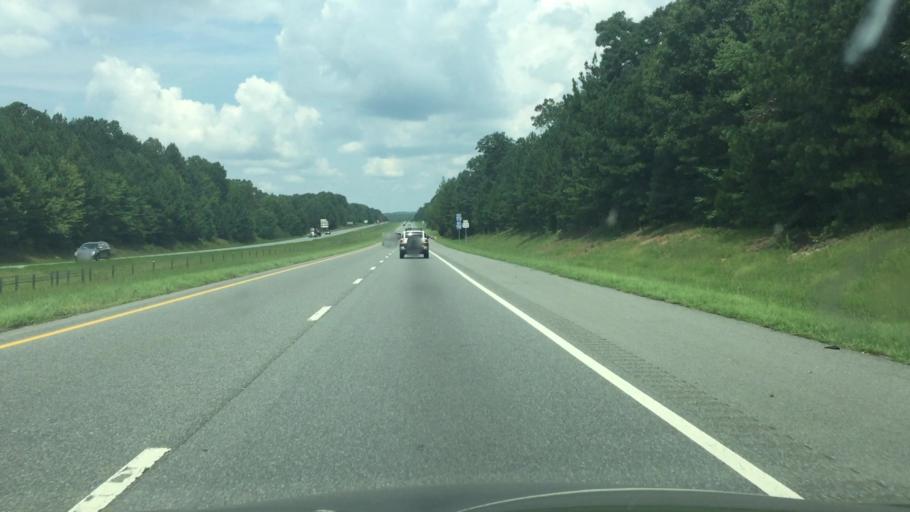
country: US
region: North Carolina
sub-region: Randolph County
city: Asheboro
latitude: 35.5423
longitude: -79.7937
